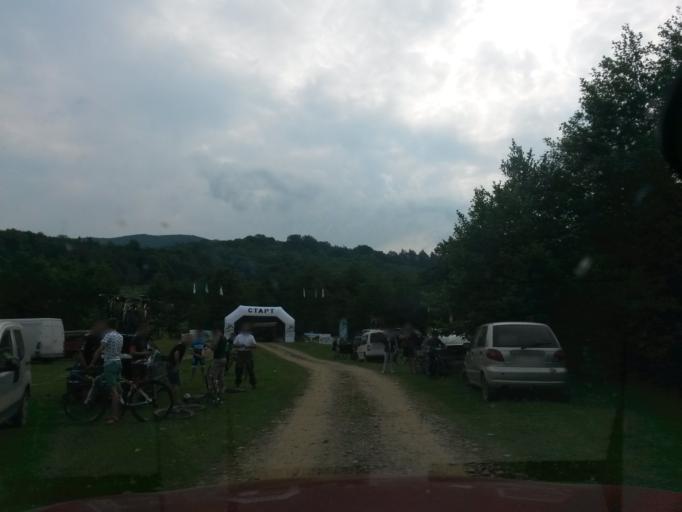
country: UA
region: Zakarpattia
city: Velykyi Bereznyi
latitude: 48.9102
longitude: 22.4809
